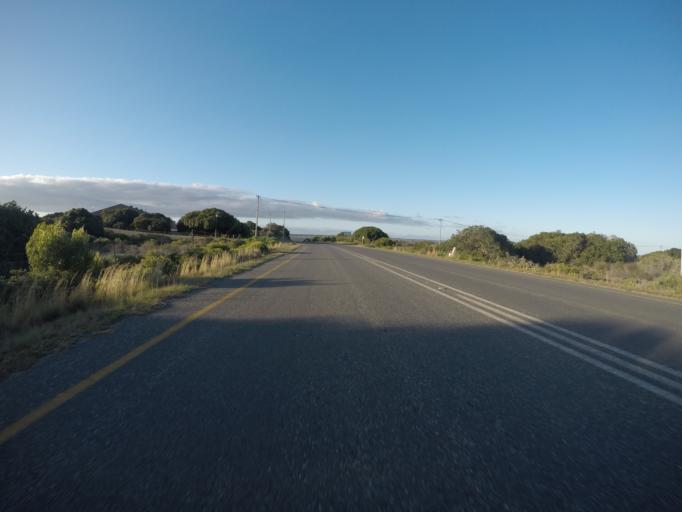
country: ZA
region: Western Cape
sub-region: Eden District Municipality
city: Riversdale
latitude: -34.3851
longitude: 21.4044
